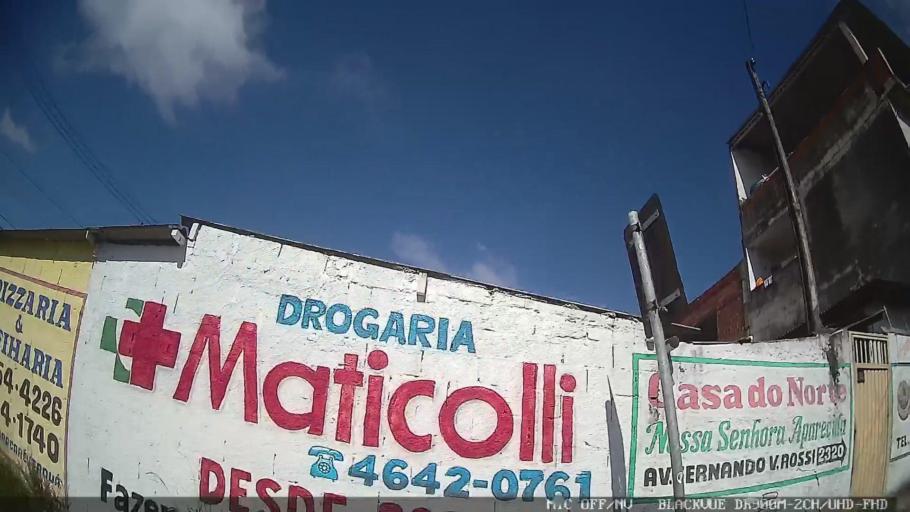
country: BR
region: Sao Paulo
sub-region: Itaquaquecetuba
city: Itaquaquecetuba
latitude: -23.5007
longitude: -46.3403
